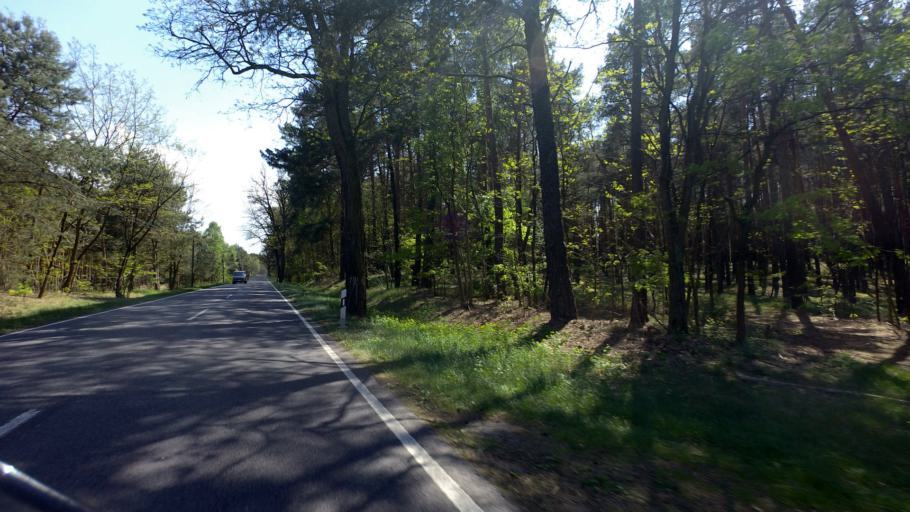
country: DE
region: Brandenburg
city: Lieberose
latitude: 52.0029
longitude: 14.1969
